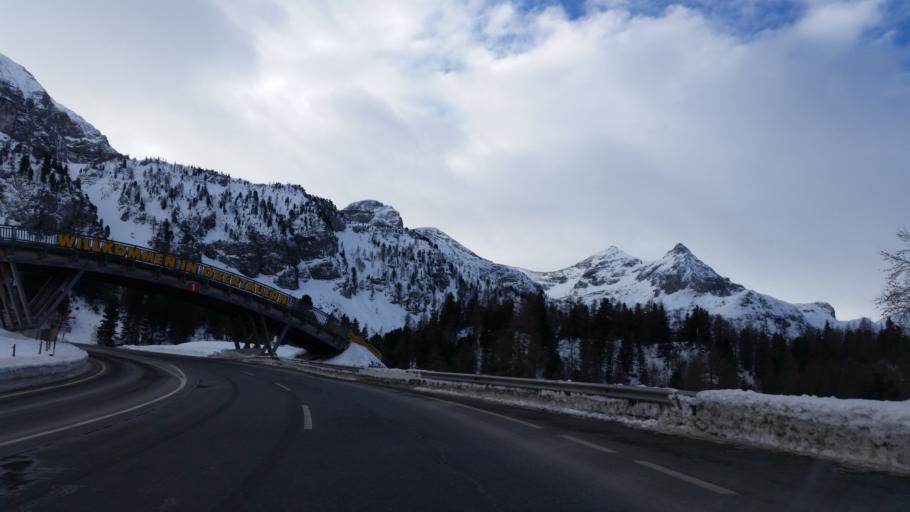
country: AT
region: Salzburg
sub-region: Politischer Bezirk Sankt Johann im Pongau
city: Untertauern
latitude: 47.2529
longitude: 13.5255
